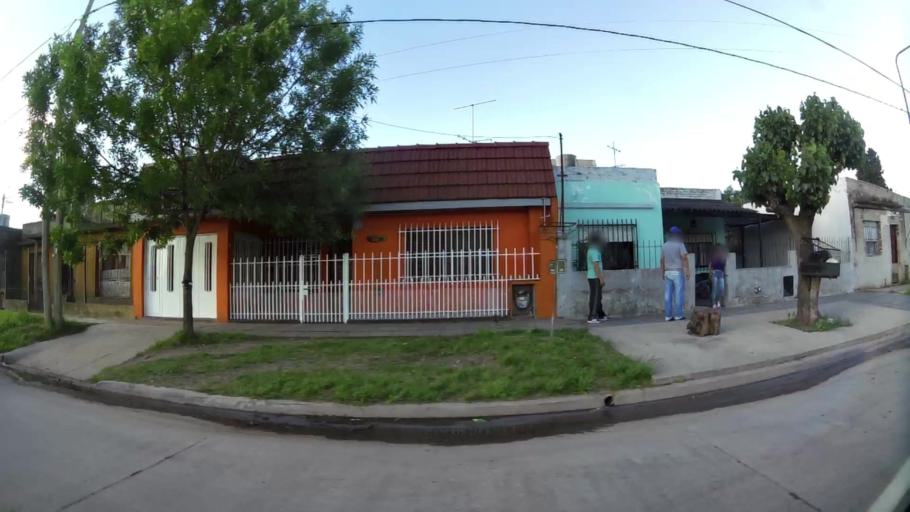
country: AR
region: Buenos Aires
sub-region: Partido de Moron
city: Moron
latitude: -34.6985
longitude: -58.6340
